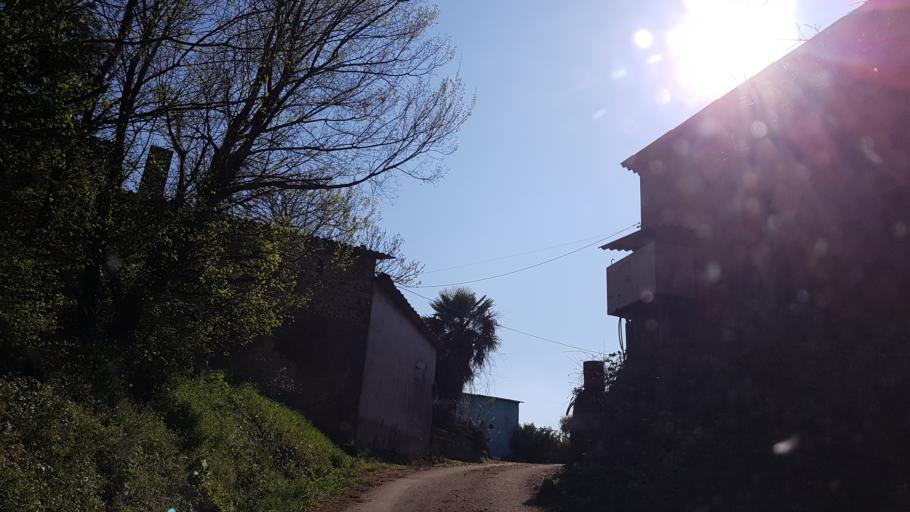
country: FR
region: Midi-Pyrenees
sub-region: Departement de l'Ariege
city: La Tour-du-Crieu
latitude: 43.0863
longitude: 1.7072
